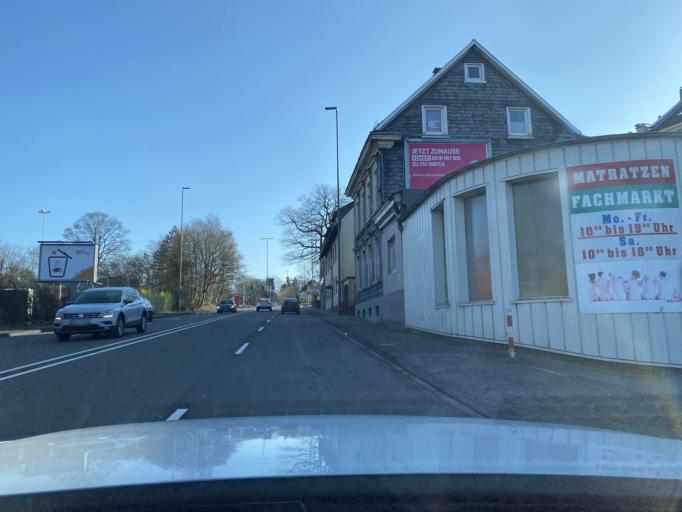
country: DE
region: North Rhine-Westphalia
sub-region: Regierungsbezirk Dusseldorf
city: Remscheid
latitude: 51.1776
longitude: 7.2203
